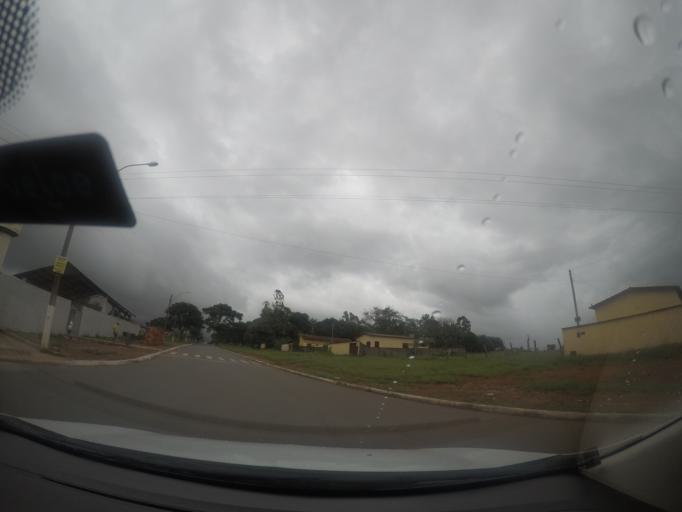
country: BR
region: Goias
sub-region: Trindade
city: Trindade
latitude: -16.6173
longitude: -49.3888
